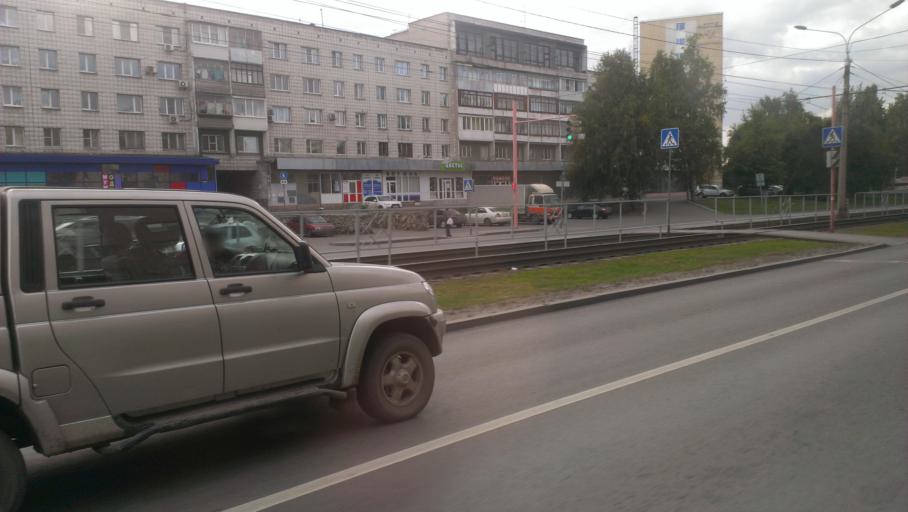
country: RU
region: Altai Krai
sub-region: Gorod Barnaulskiy
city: Barnaul
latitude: 53.3466
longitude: 83.7644
